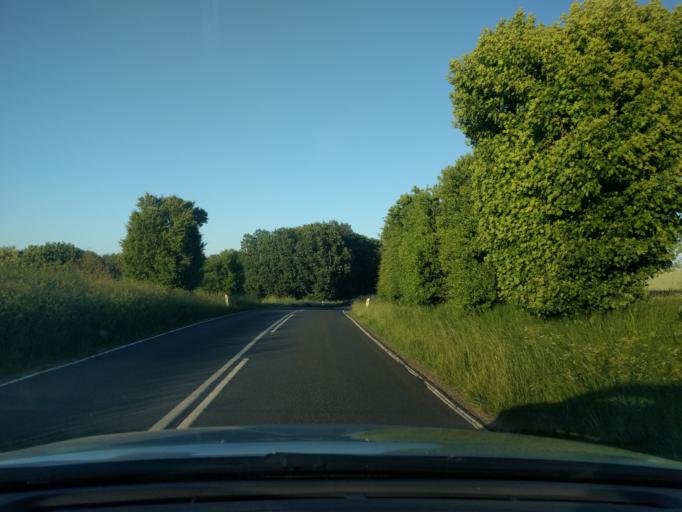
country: DK
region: South Denmark
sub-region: Kerteminde Kommune
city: Kerteminde
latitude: 55.5351
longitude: 10.6556
